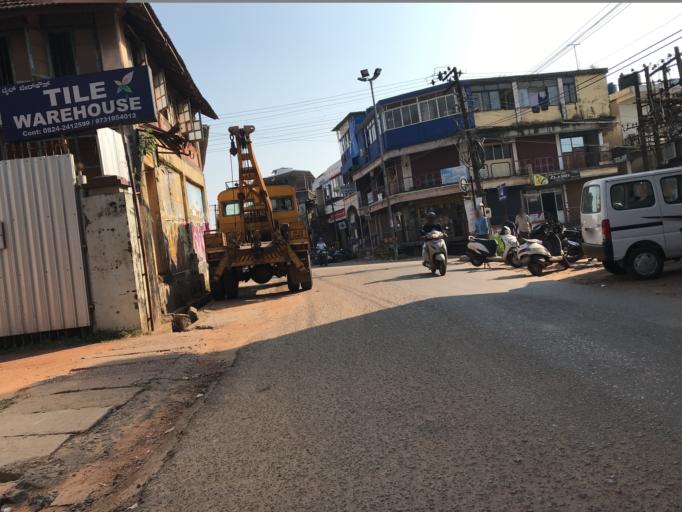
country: IN
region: Karnataka
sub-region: Dakshina Kannada
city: Ullal
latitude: 12.8621
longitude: 74.8336
